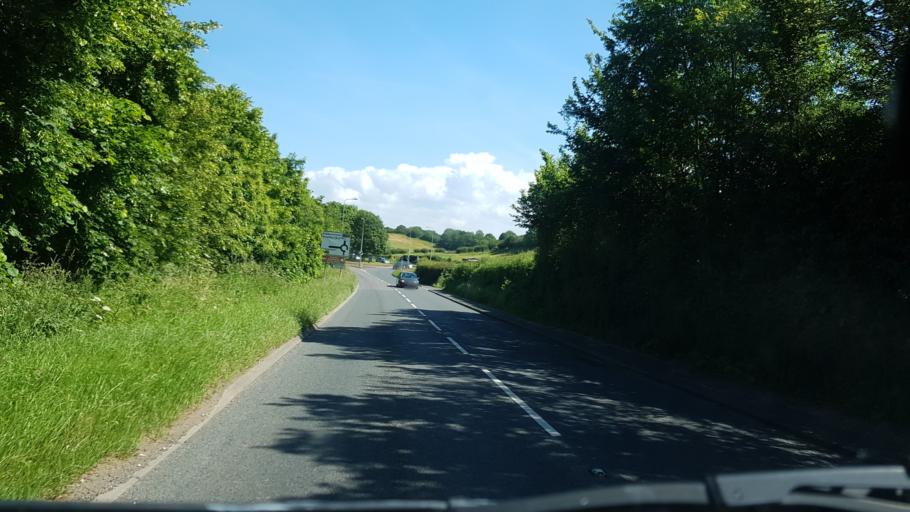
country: GB
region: England
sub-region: Worcestershire
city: Bewdley
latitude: 52.3647
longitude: -2.3015
